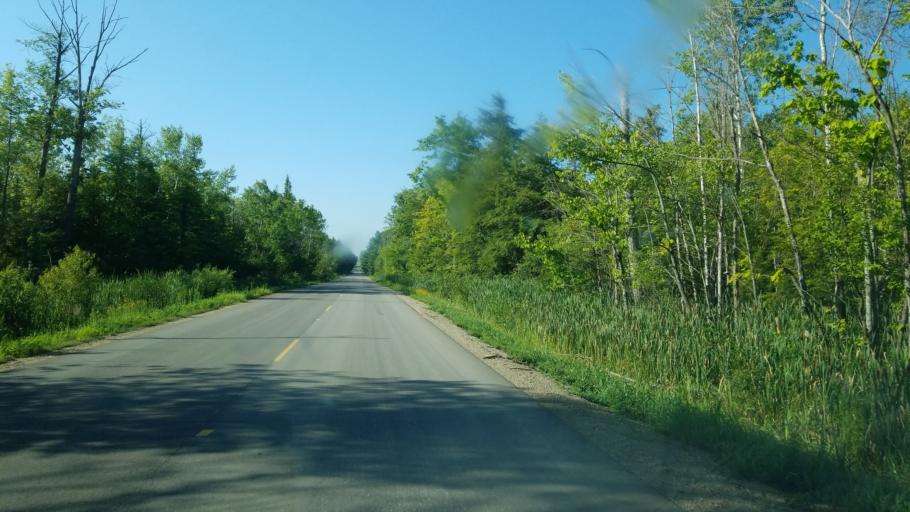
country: US
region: Michigan
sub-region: Mecosta County
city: Canadian Lakes
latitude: 43.5119
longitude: -85.3930
